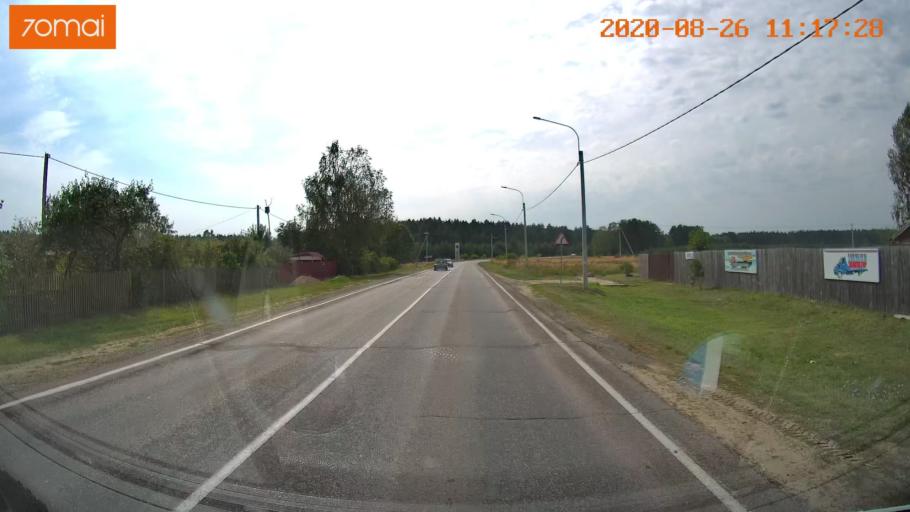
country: RU
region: Rjazan
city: Shilovo
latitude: 54.4187
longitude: 41.1102
